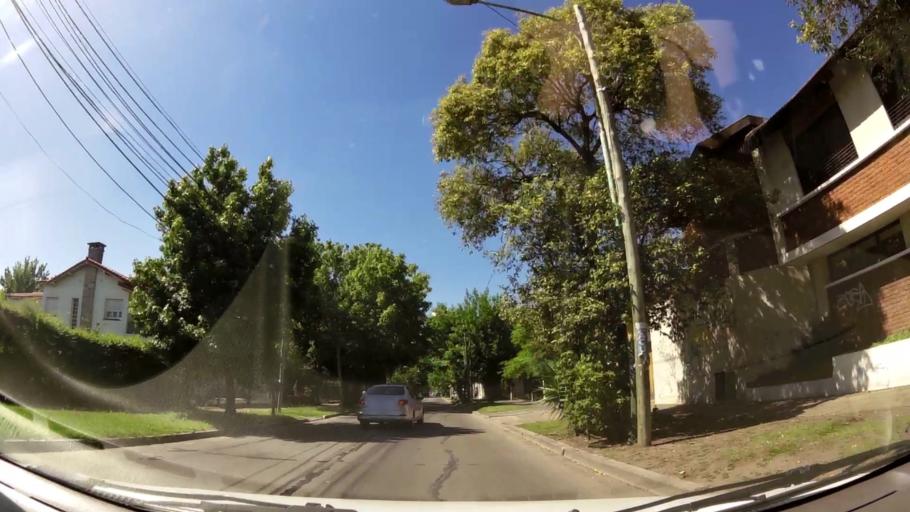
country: AR
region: Buenos Aires
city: Ituzaingo
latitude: -34.6505
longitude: -58.6634
